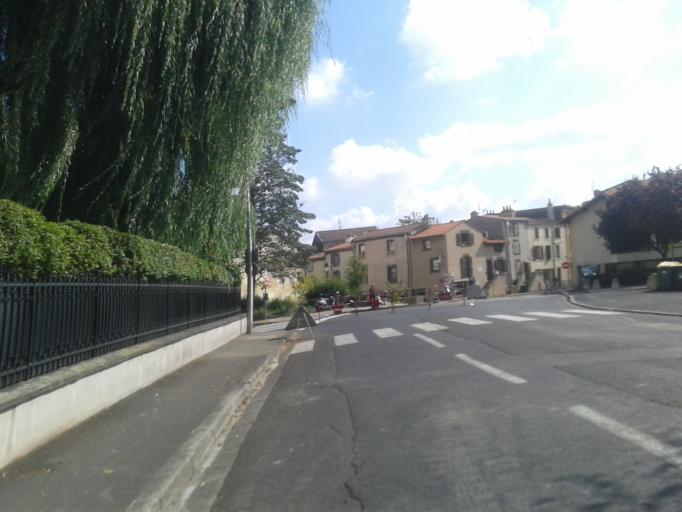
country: FR
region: Auvergne
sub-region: Departement du Puy-de-Dome
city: Chamalieres
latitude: 45.7762
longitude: 3.0645
